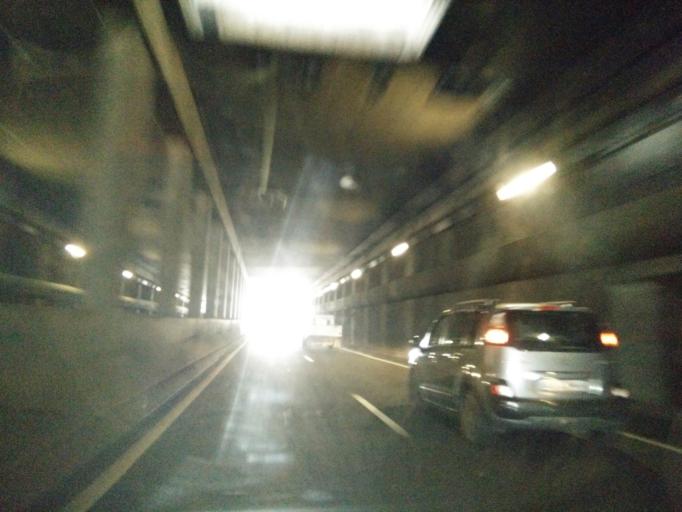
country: MQ
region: Martinique
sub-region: Martinique
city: Fort-de-France
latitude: 14.6150
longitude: -61.0621
